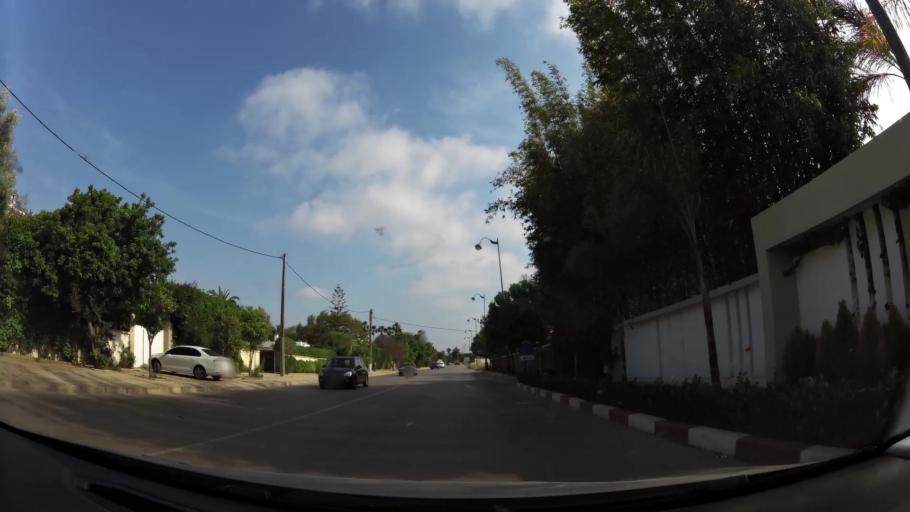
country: MA
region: Rabat-Sale-Zemmour-Zaer
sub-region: Rabat
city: Rabat
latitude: 33.9636
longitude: -6.8375
